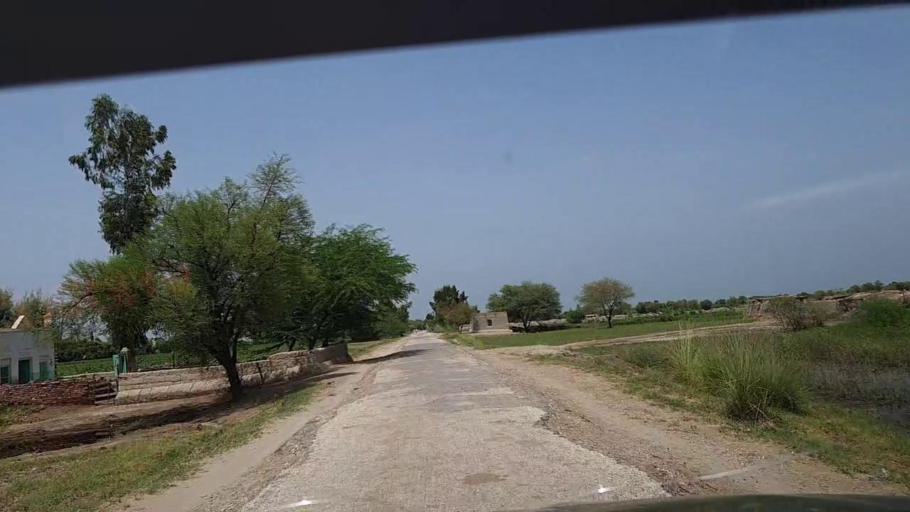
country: PK
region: Sindh
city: Khanpur
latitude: 27.8060
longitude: 69.4506
